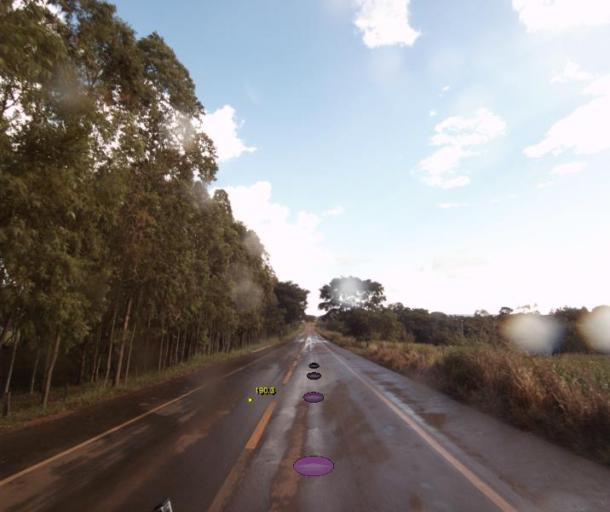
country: BR
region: Goias
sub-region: Itaberai
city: Itaberai
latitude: -16.0353
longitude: -49.7839
